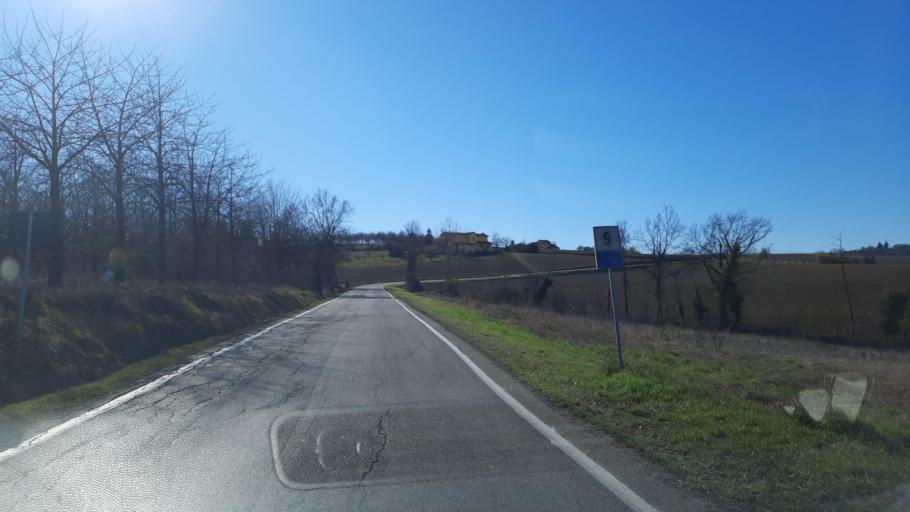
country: IT
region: Piedmont
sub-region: Provincia di Alessandria
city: Frassinello Monferrato
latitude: 45.0412
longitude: 8.3835
